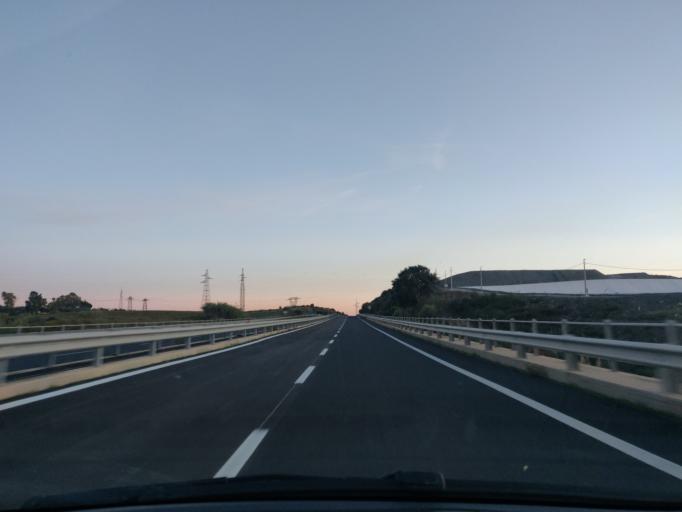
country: IT
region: Latium
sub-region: Citta metropolitana di Roma Capitale
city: Aurelia
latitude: 42.1182
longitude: 11.7914
